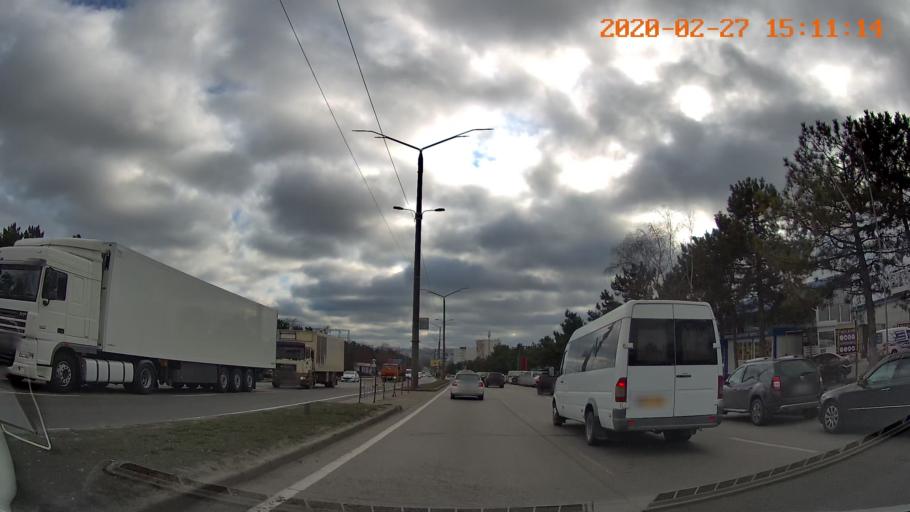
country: MD
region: Chisinau
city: Stauceni
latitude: 47.0610
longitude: 28.8543
